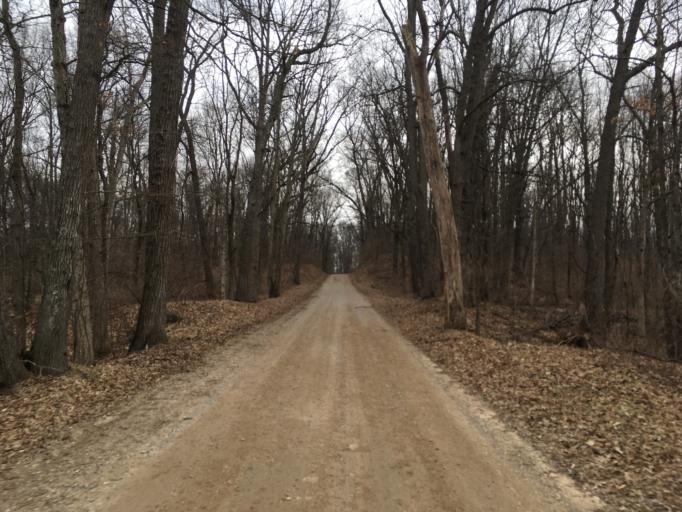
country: US
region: Michigan
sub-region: Jackson County
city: Grass Lake
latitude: 42.3230
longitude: -84.1950
